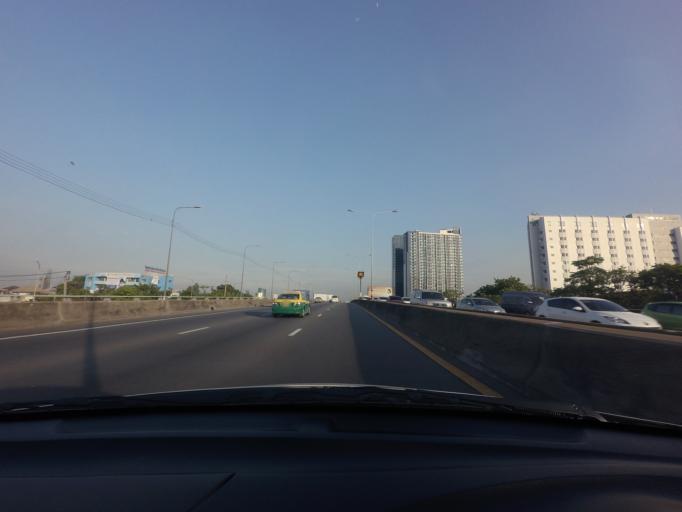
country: TH
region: Bangkok
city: Chatuchak
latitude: 13.8338
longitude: 100.5391
